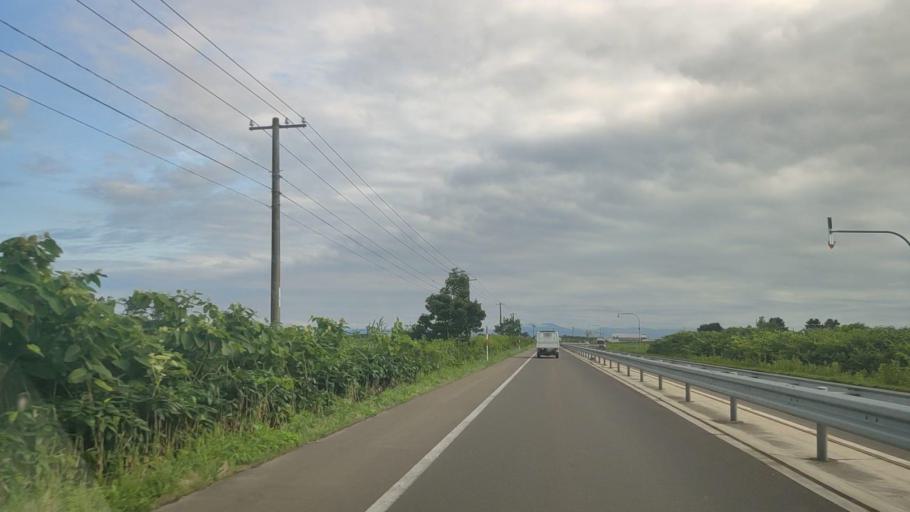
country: JP
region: Hokkaido
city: Niseko Town
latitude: 42.4518
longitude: 140.3317
